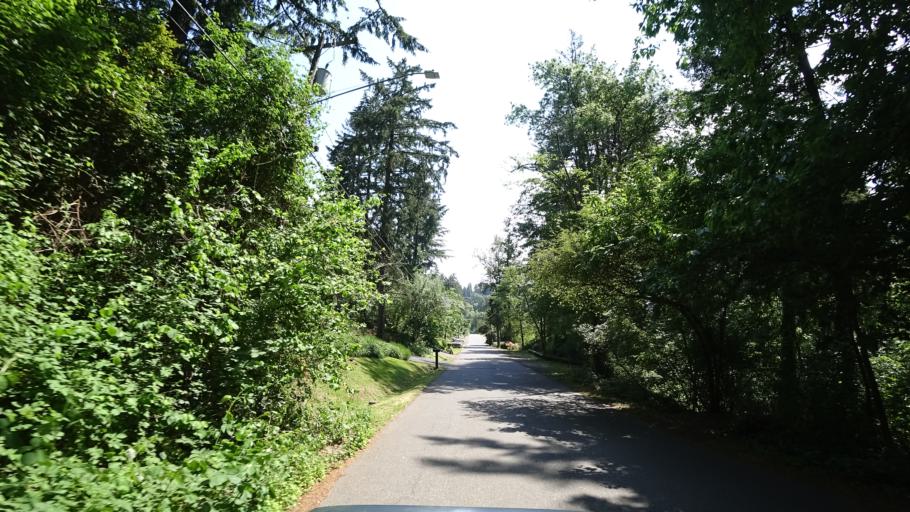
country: US
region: Oregon
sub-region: Washington County
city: Metzger
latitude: 45.4508
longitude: -122.7334
